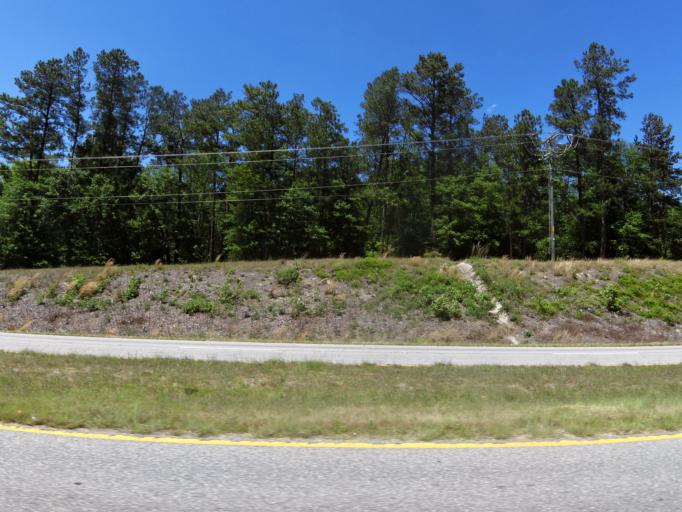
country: US
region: South Carolina
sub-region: Aiken County
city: Clearwater
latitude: 33.5065
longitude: -81.8882
